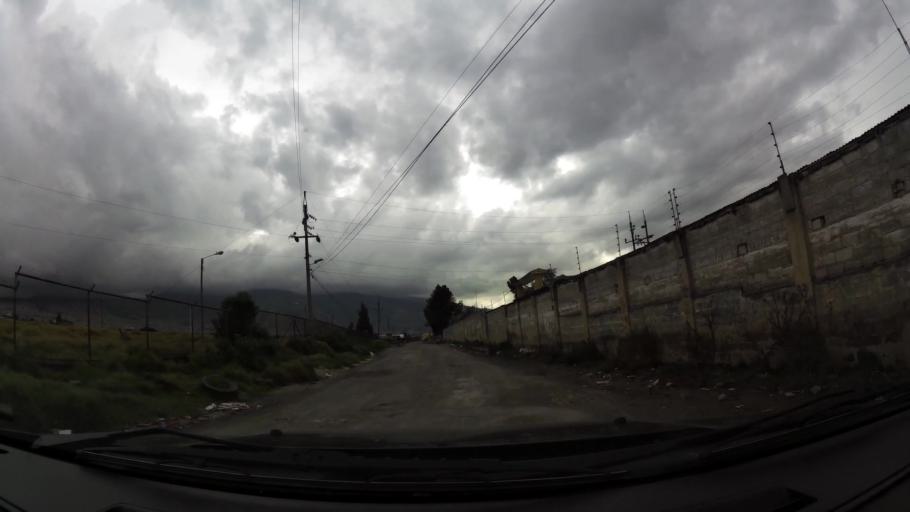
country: EC
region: Pichincha
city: Quito
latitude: -0.3131
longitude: -78.5385
